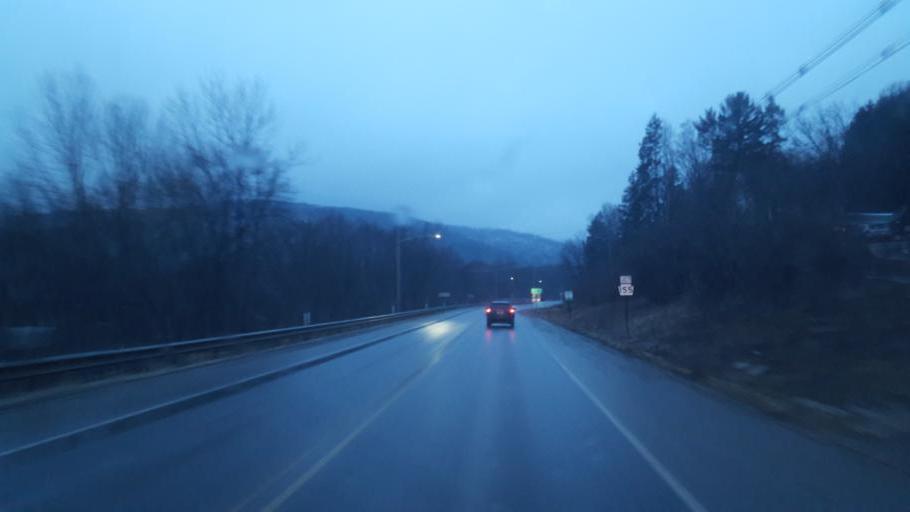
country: US
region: Pennsylvania
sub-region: McKean County
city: Port Allegany
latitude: 41.8045
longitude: -78.2743
